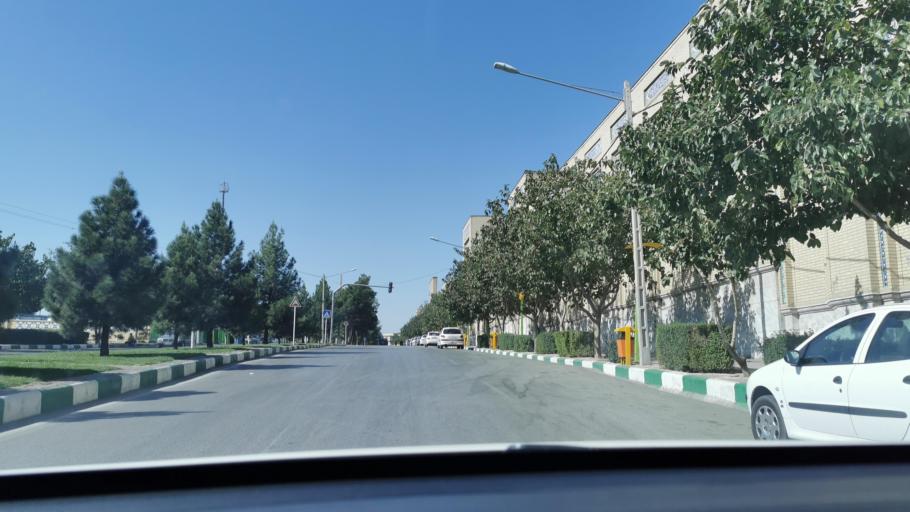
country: IR
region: Razavi Khorasan
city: Mashhad
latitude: 36.3427
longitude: 59.6317
